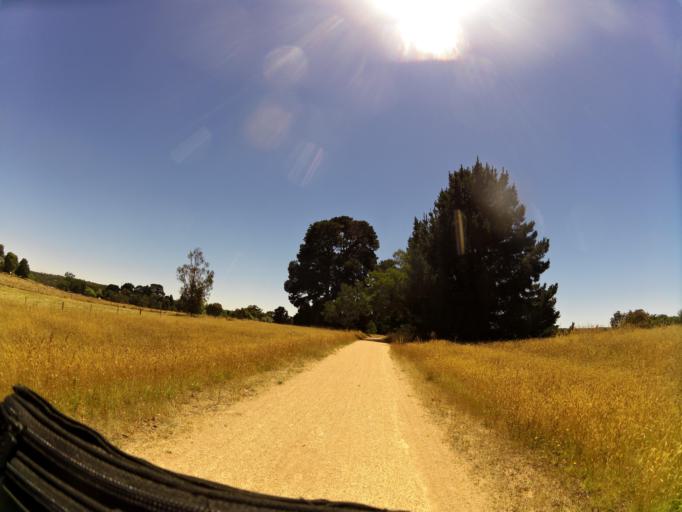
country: AU
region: Victoria
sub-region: Ballarat North
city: Delacombe
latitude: -37.6638
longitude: 143.6609
